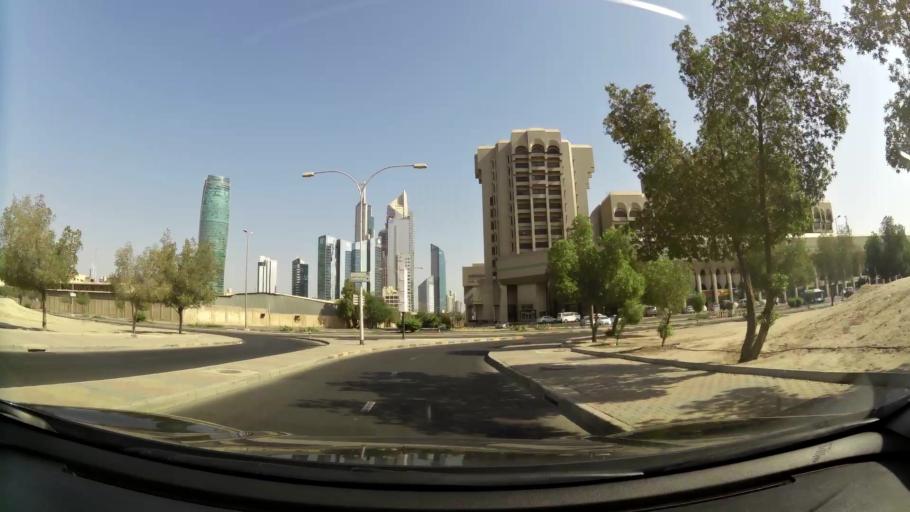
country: KW
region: Al Asimah
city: Kuwait City
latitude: 29.3688
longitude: 47.9862
